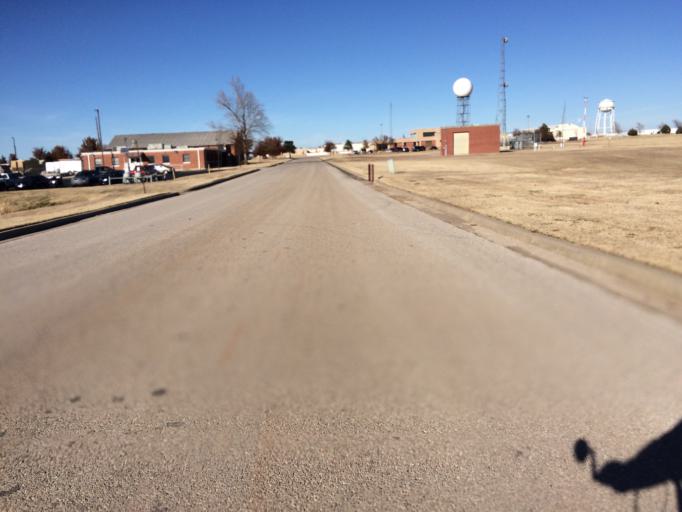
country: US
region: Oklahoma
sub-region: Cleveland County
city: Norman
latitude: 35.2350
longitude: -97.4613
